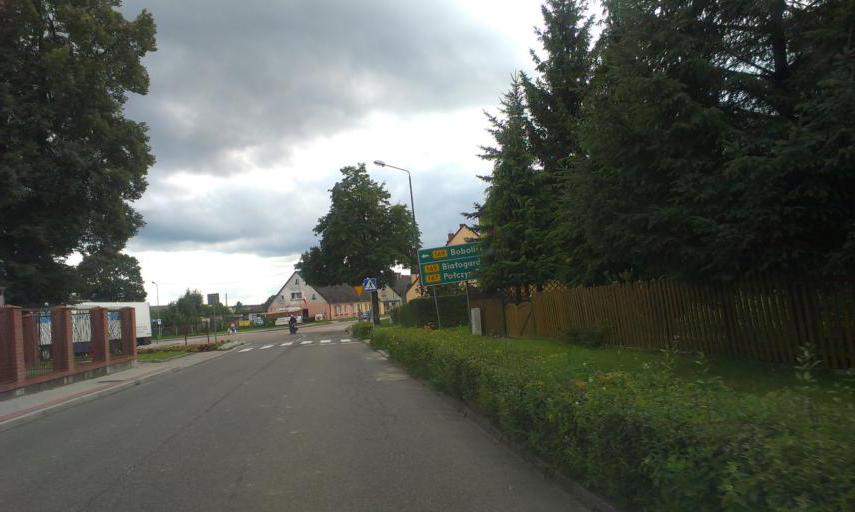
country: PL
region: West Pomeranian Voivodeship
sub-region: Powiat bialogardzki
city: Tychowo
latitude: 53.9277
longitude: 16.2566
